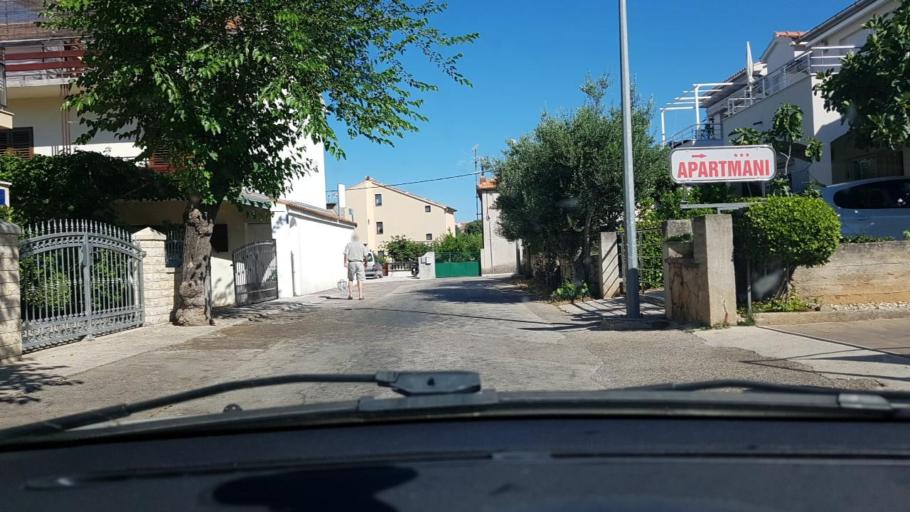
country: HR
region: Sibensko-Kniniska
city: Vodice
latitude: 43.7600
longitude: 15.7802
